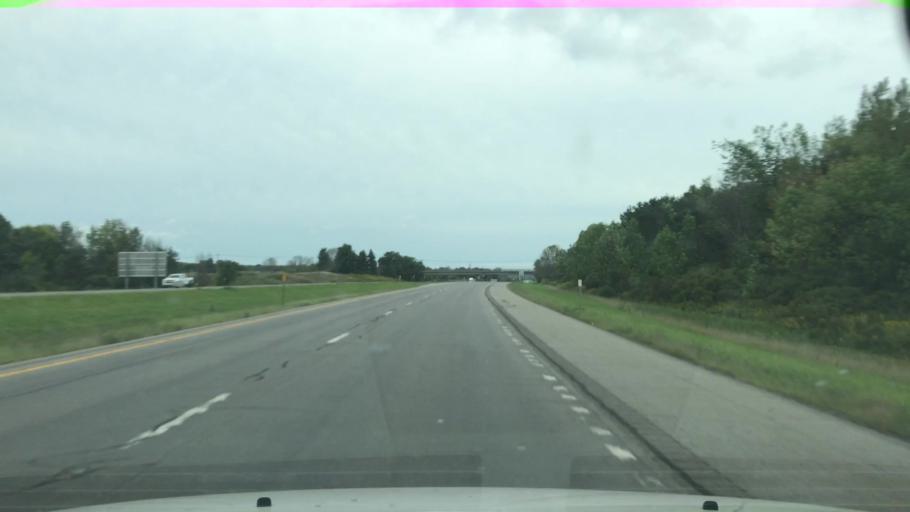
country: US
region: New York
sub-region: Erie County
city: Orchard Park
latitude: 42.7394
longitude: -78.7640
